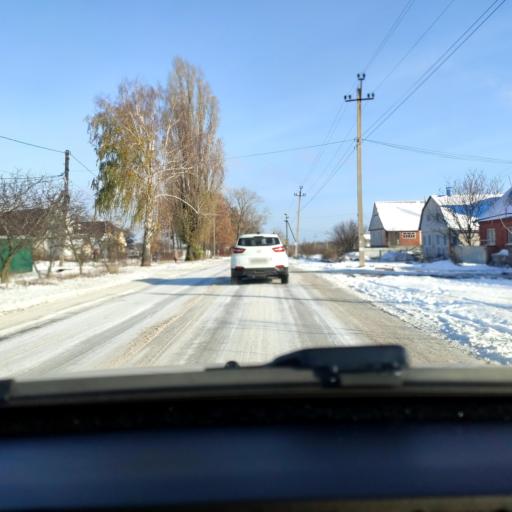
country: RU
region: Voronezj
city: Devitsa
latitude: 51.6030
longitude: 38.9800
